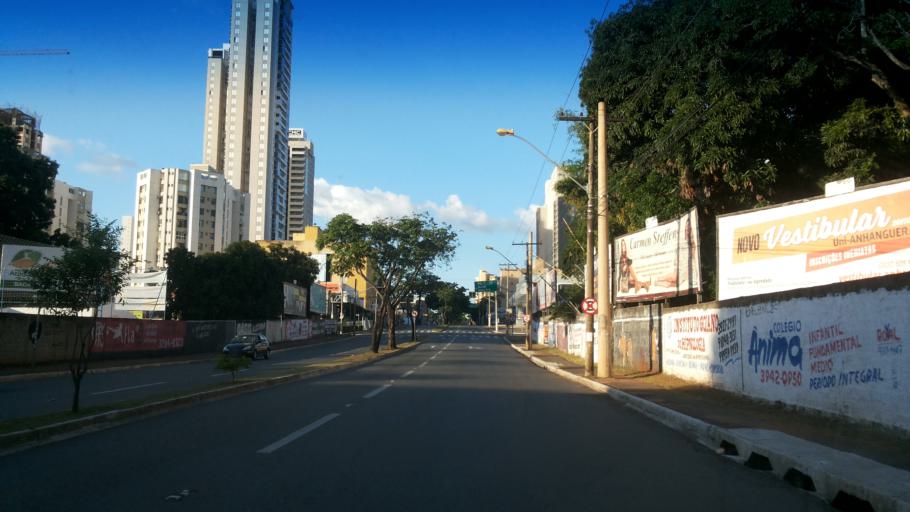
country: BR
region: Goias
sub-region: Goiania
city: Goiania
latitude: -16.7049
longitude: -49.2761
